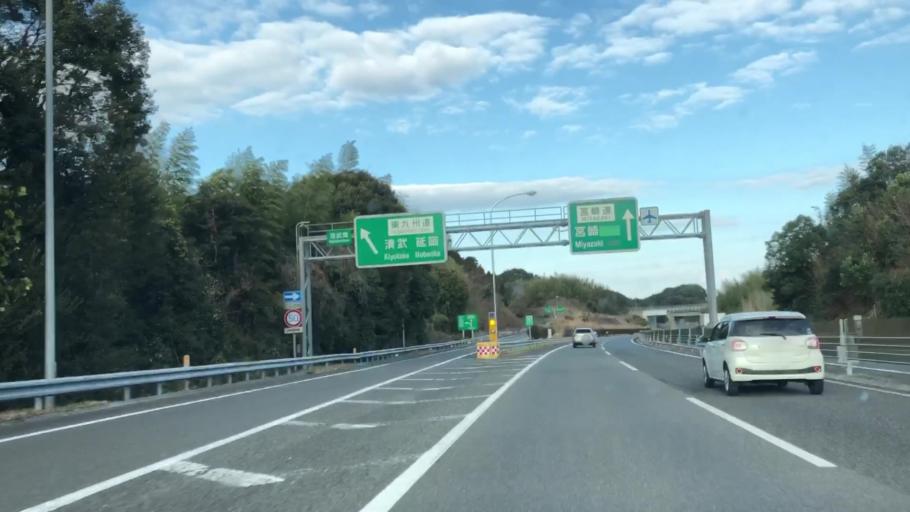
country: JP
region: Miyazaki
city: Miyazaki-shi
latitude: 31.8464
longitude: 131.3540
